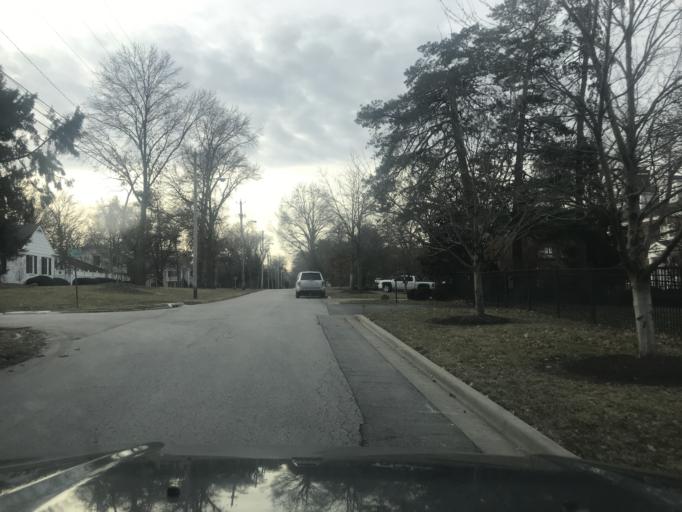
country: US
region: Kansas
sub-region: Johnson County
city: Westwood
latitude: 39.0328
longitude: -94.5993
